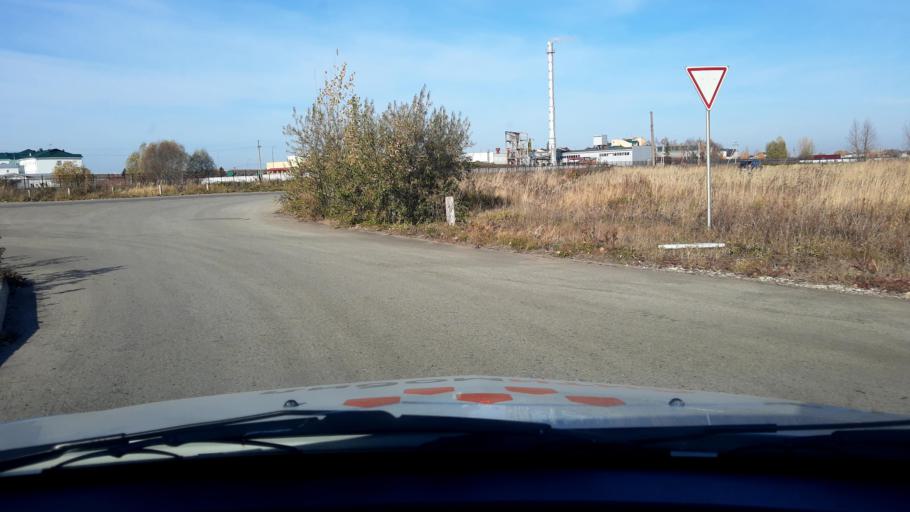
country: RU
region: Bashkortostan
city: Kabakovo
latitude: 54.7385
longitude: 56.2037
